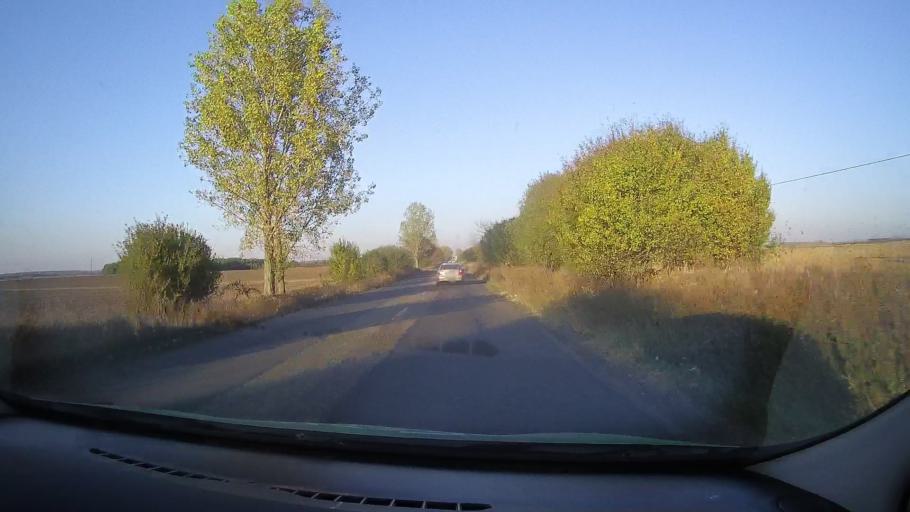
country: RO
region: Bihor
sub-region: Comuna Salard
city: Salard
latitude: 47.2040
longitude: 22.0129
